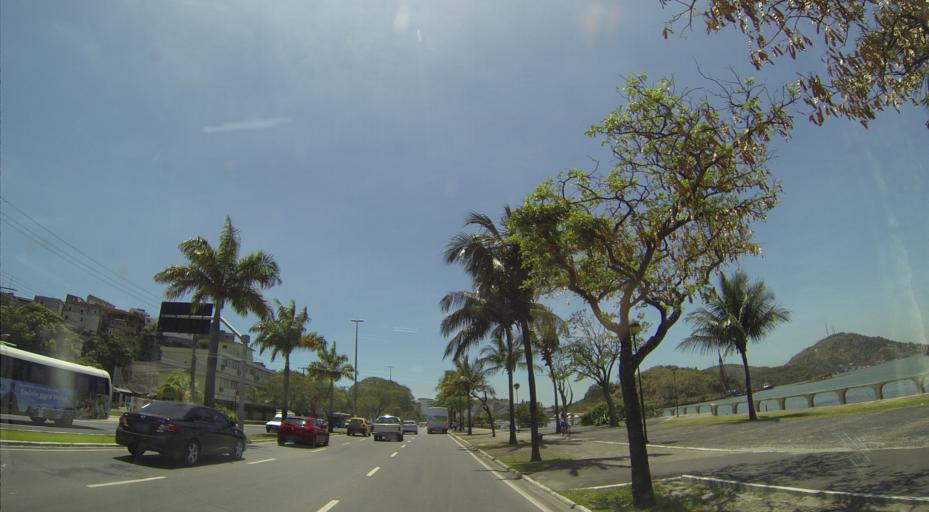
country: BR
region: Espirito Santo
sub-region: Vitoria
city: Vitoria
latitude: -20.3177
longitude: -40.3186
